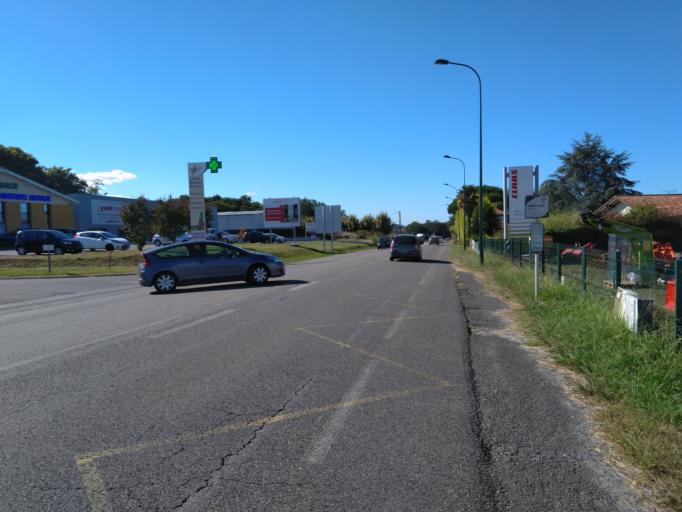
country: FR
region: Aquitaine
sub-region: Departement des Landes
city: Narrosse
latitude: 43.6984
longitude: -1.0236
